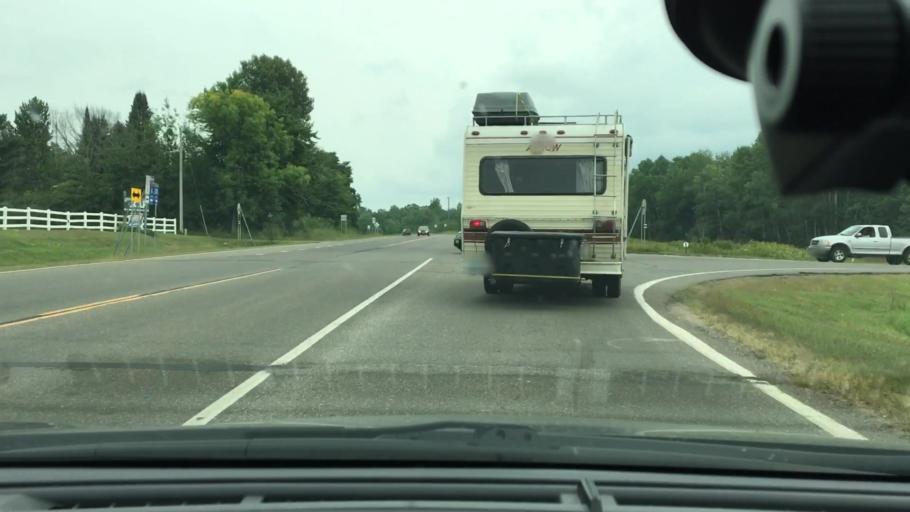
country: US
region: Minnesota
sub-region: Crow Wing County
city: Crosby
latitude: 46.4752
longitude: -93.8931
